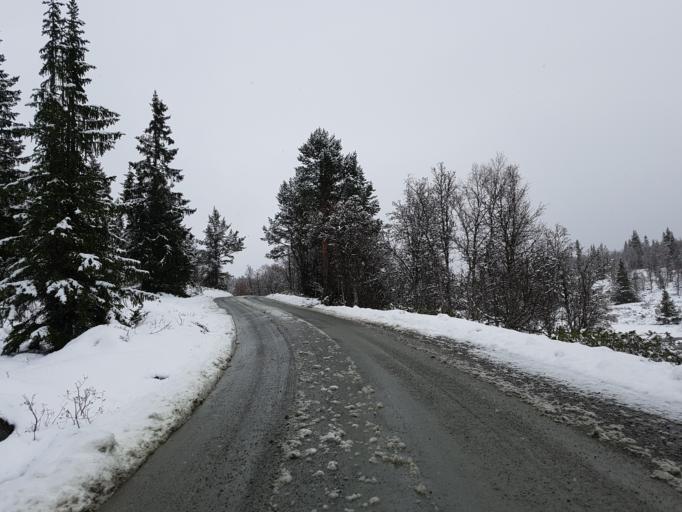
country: NO
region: Oppland
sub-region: Sel
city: Otta
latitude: 61.8026
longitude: 9.7015
